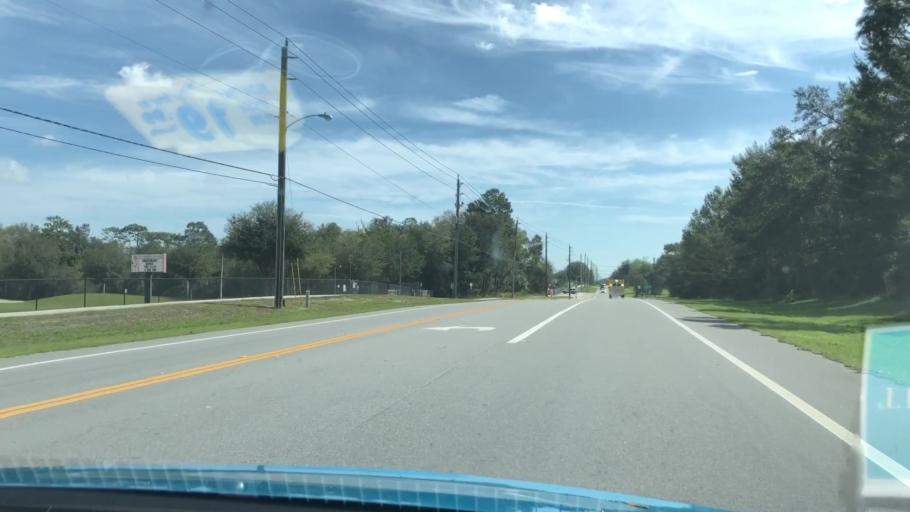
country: US
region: Florida
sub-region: Seminole County
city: Midway
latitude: 28.8532
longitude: -81.1758
